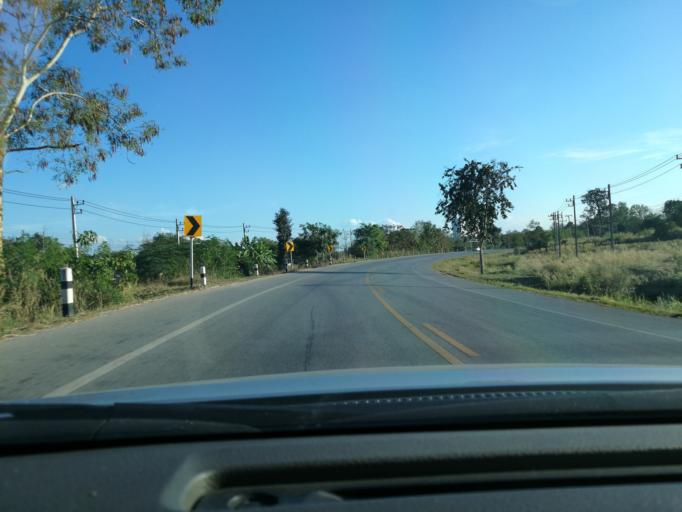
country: TH
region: Phitsanulok
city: Nakhon Thai
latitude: 17.0547
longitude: 100.8111
